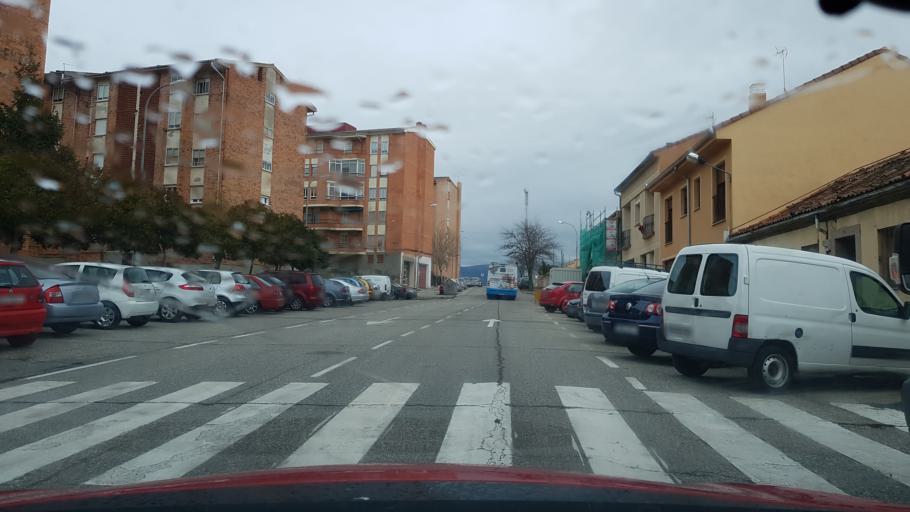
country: ES
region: Castille and Leon
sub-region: Provincia de Segovia
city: Segovia
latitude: 40.9436
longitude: -4.1023
